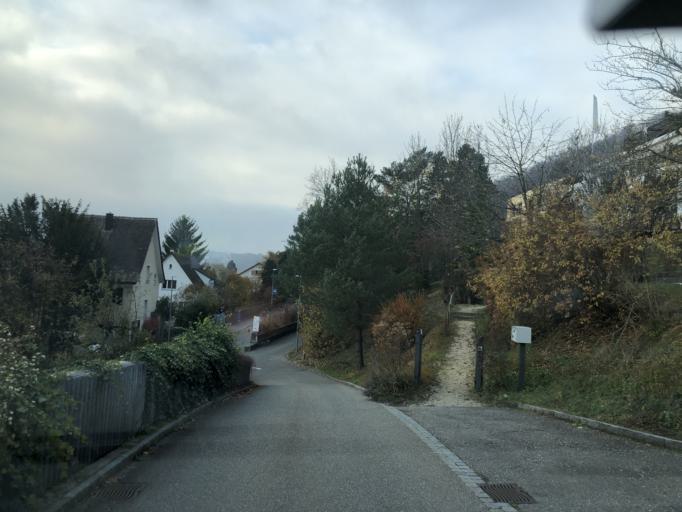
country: CH
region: Aargau
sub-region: Bezirk Baden
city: Wettingen
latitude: 47.4705
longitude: 8.3296
